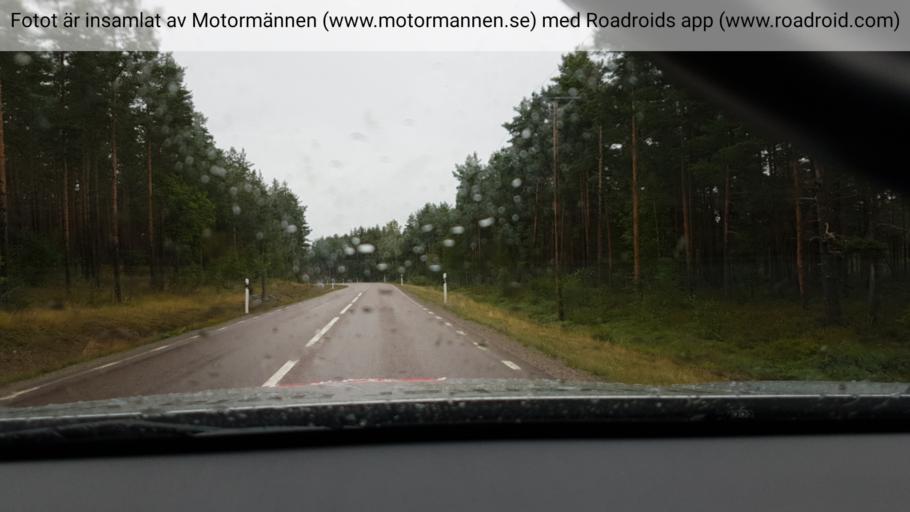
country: SE
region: Gaevleborg
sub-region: Gavle Kommun
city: Hedesunda
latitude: 60.5226
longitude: 16.9450
